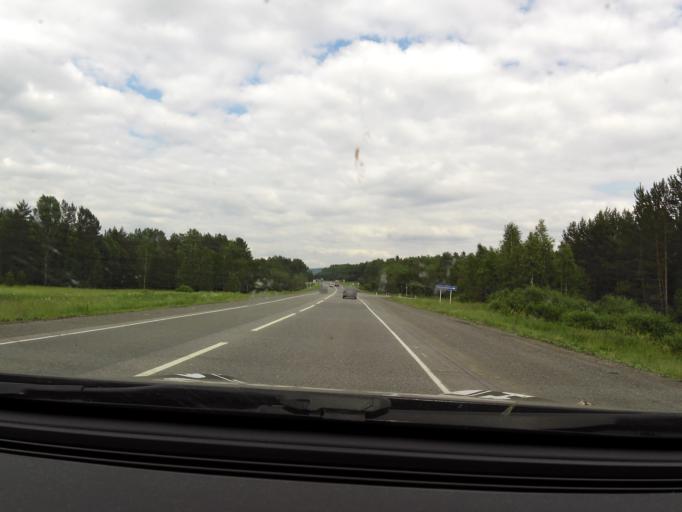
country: RU
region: Sverdlovsk
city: Druzhinino
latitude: 56.8315
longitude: 59.6234
